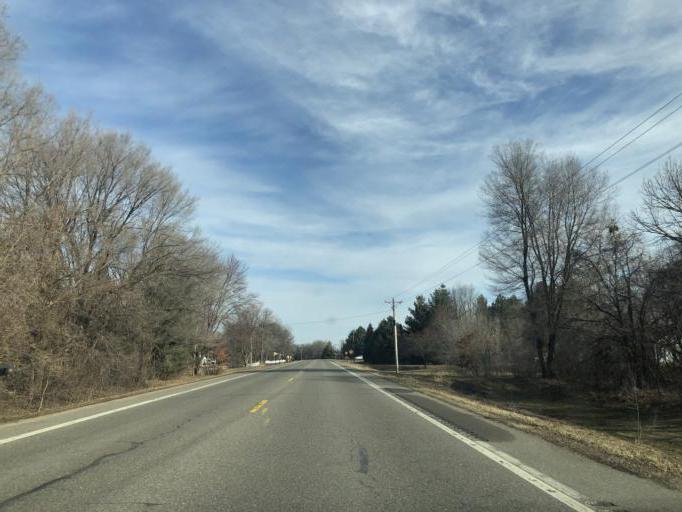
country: US
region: Minnesota
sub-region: Sherburne County
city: Becker
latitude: 45.4160
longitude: -93.8709
